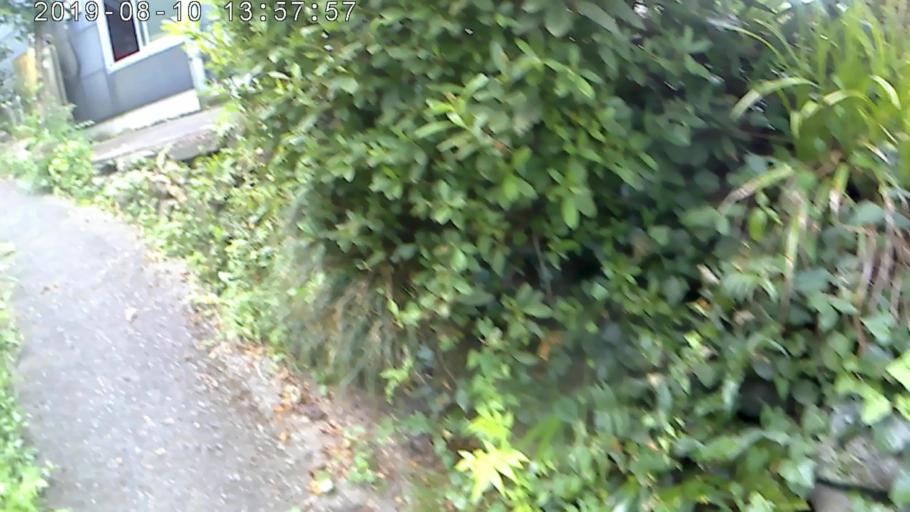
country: JP
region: Yamanashi
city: Uenohara
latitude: 35.6324
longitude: 139.1051
